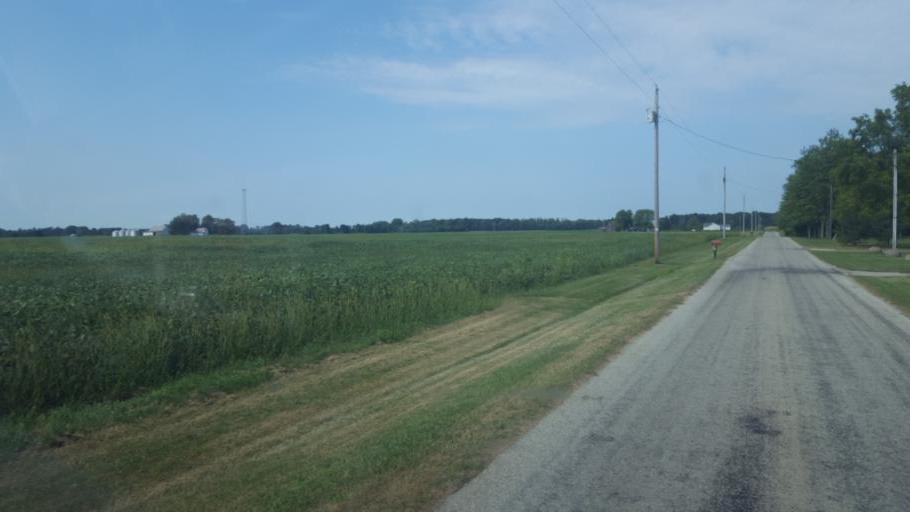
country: US
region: Ohio
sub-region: Delaware County
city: Ashley
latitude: 40.4819
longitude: -83.0011
